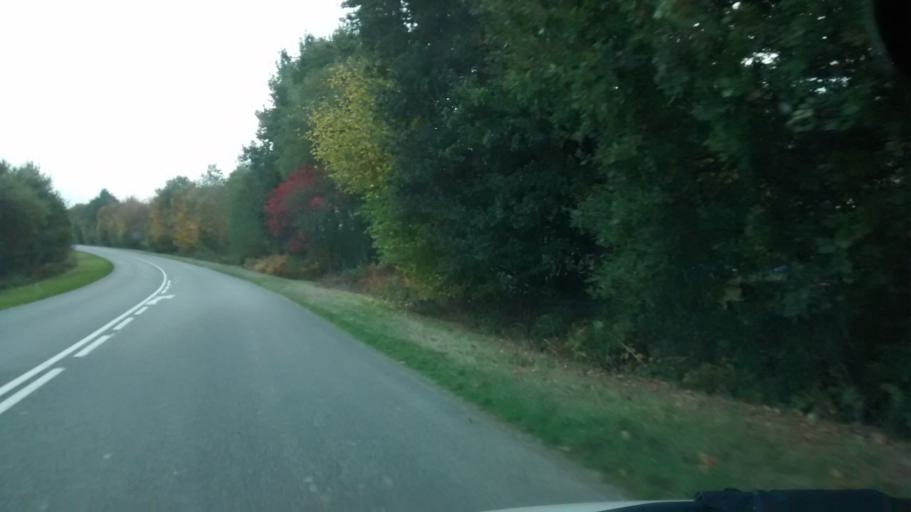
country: FR
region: Brittany
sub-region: Departement d'Ille-et-Vilaine
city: Acigne
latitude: 48.1585
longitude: -1.5169
